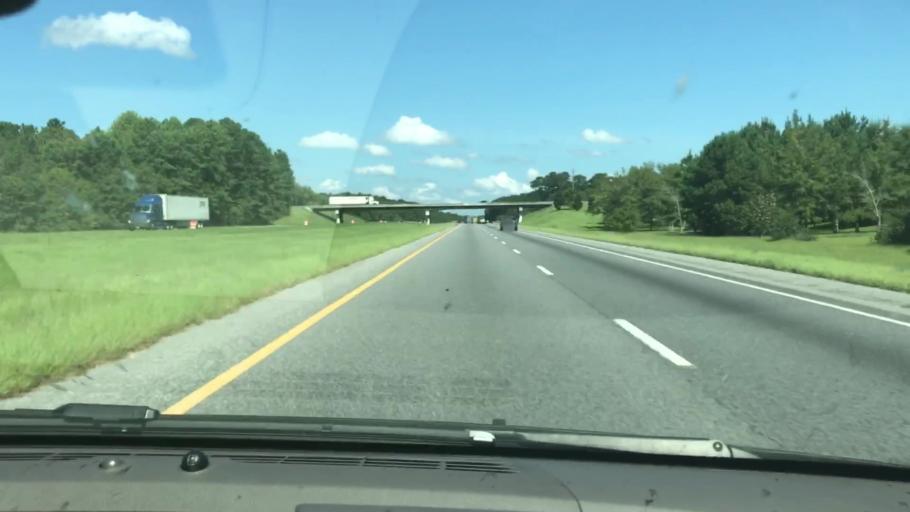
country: US
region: Georgia
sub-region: Harris County
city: Hamilton
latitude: 32.6603
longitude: -84.9785
